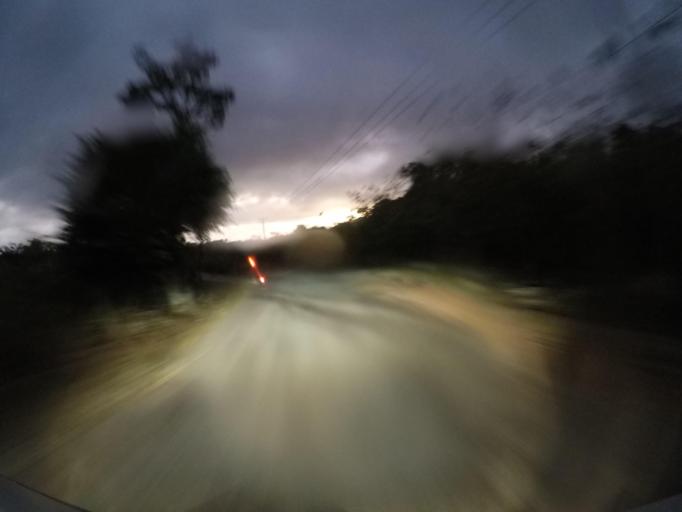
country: TL
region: Lautem
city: Lospalos
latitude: -8.4260
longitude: 127.0043
